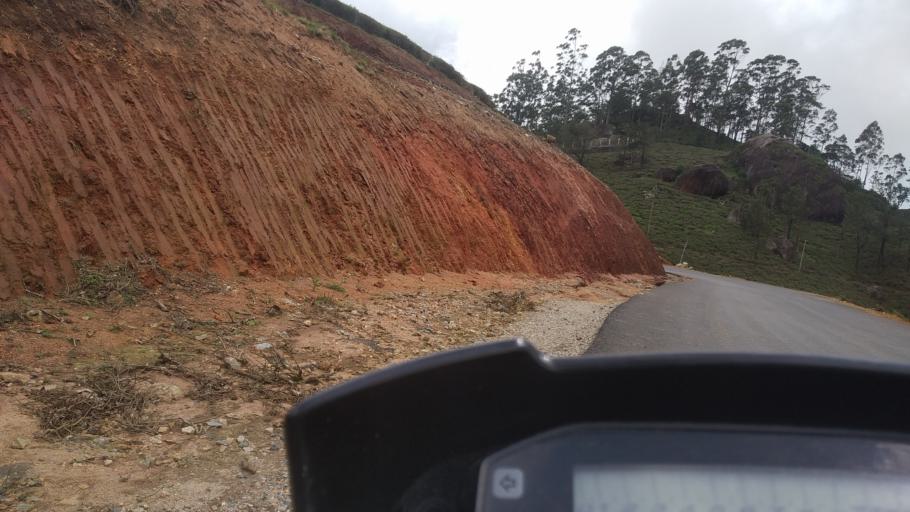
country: IN
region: Kerala
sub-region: Idukki
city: Munnar
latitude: 10.0360
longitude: 77.1575
